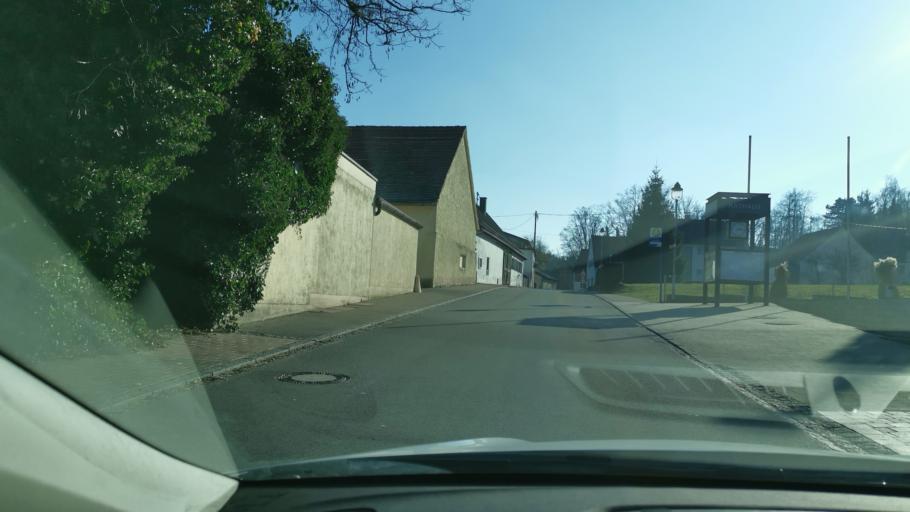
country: DE
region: Bavaria
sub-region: Swabia
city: Aindling
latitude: 48.5123
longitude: 10.9530
